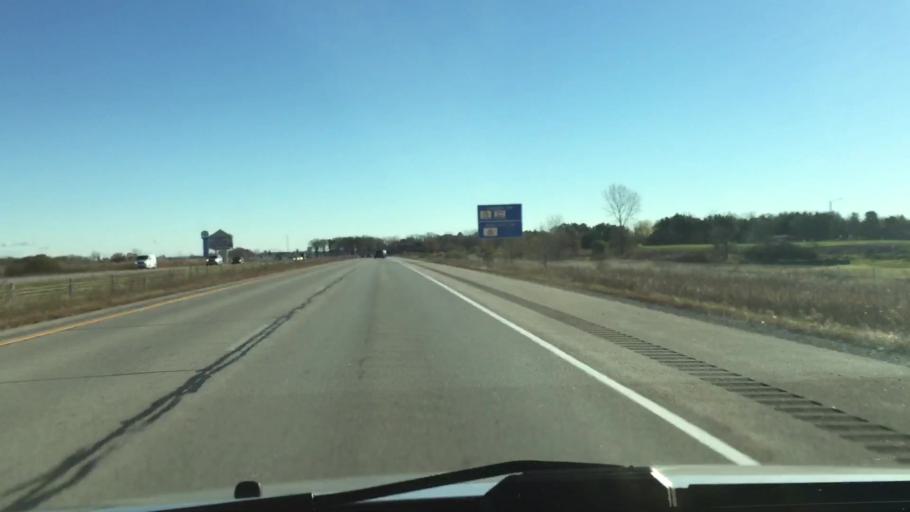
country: US
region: Wisconsin
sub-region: Outagamie County
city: Kaukauna
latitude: 44.2977
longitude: -88.2866
